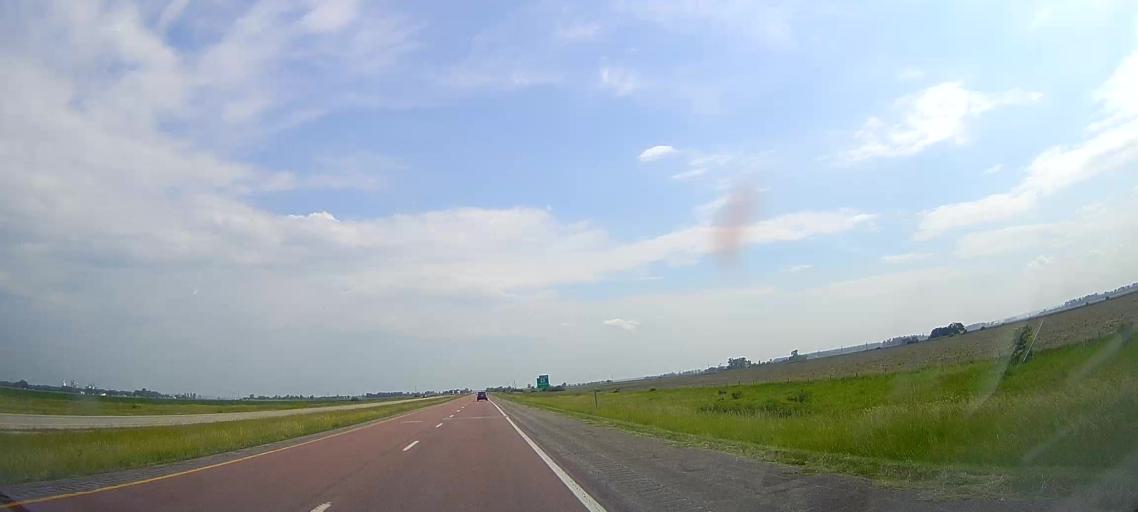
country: US
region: Iowa
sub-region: Monona County
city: Onawa
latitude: 41.9503
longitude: -96.1037
